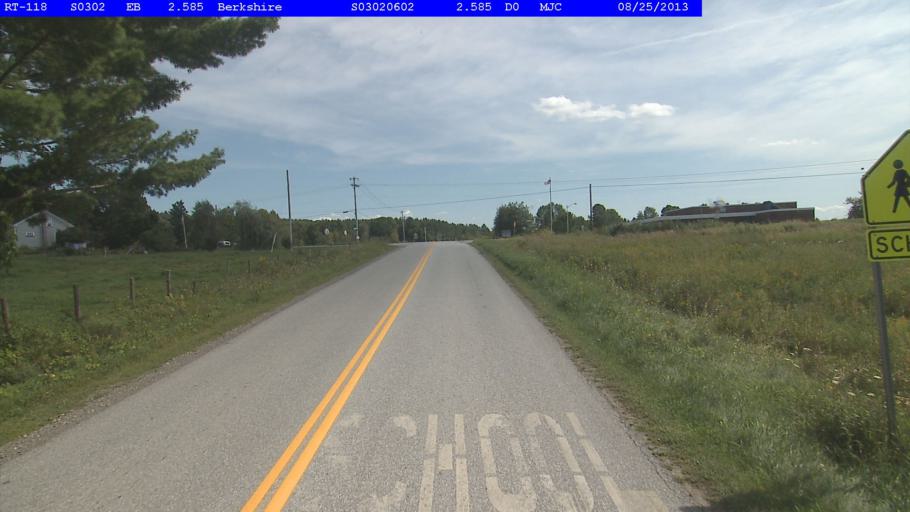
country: US
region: Vermont
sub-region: Franklin County
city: Enosburg Falls
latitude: 44.9738
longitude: -72.7669
